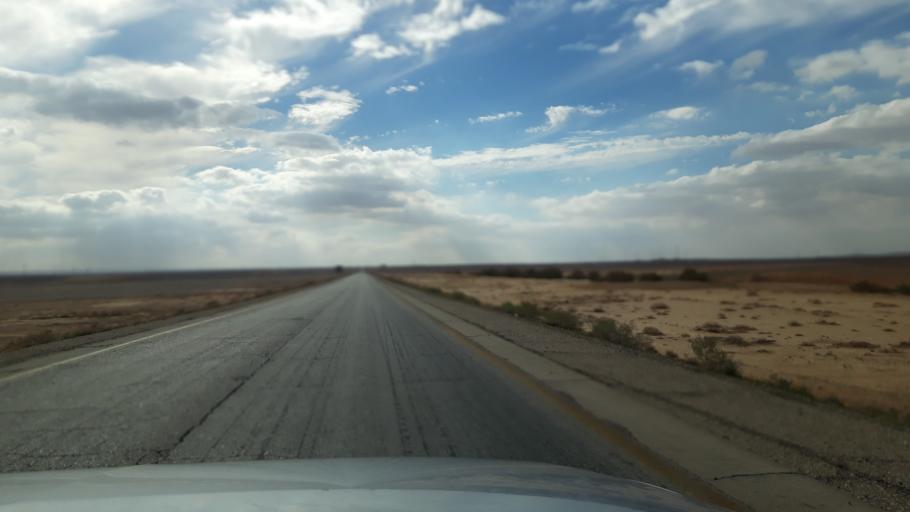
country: JO
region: Amman
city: Al Azraq ash Shamali
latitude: 31.7313
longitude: 36.5026
